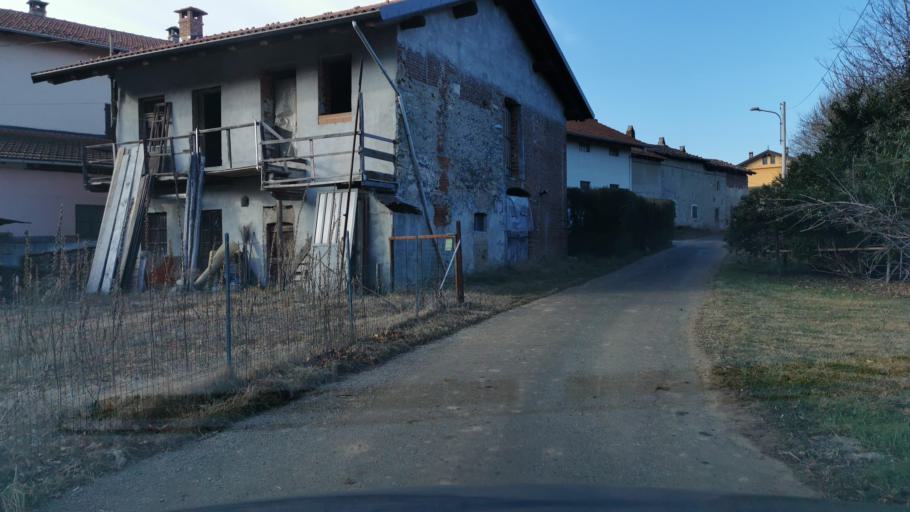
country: IT
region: Piedmont
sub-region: Provincia di Torino
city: Rocca Canavese
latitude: 45.2873
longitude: 7.5724
